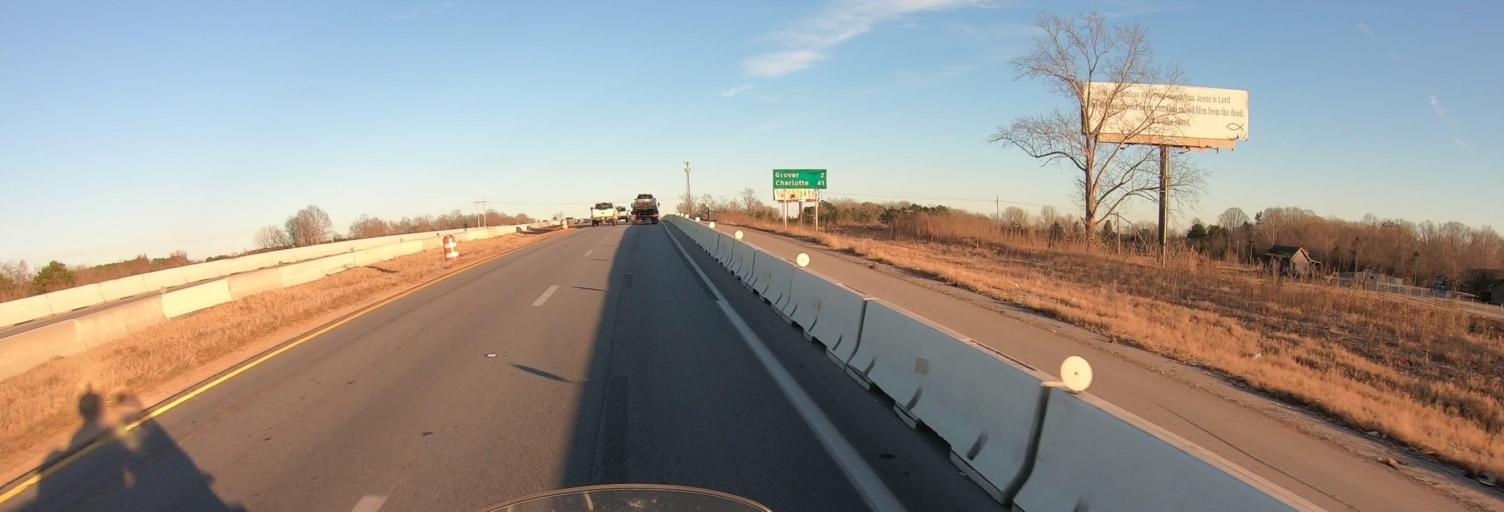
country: US
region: South Carolina
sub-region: Cherokee County
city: Blacksburg
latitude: 35.1586
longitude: -81.4690
